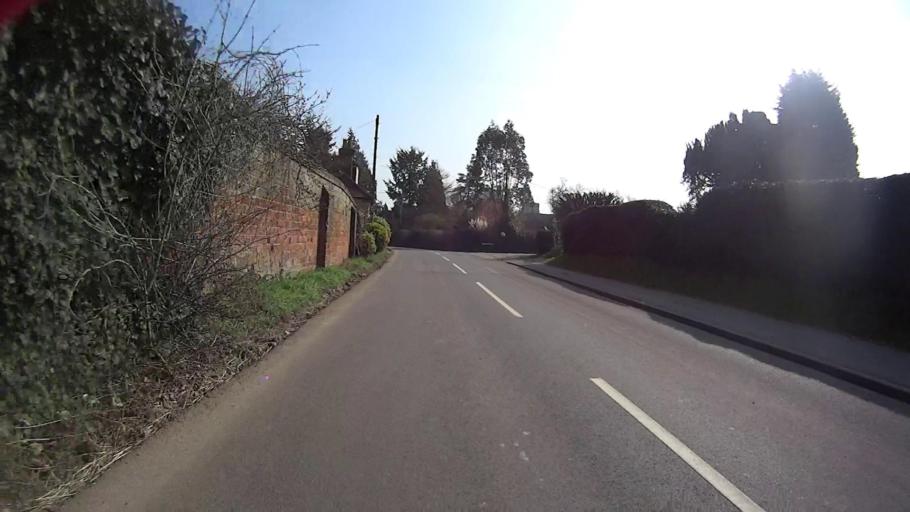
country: GB
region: England
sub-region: Surrey
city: Headley
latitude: 51.2350
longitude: -0.2676
